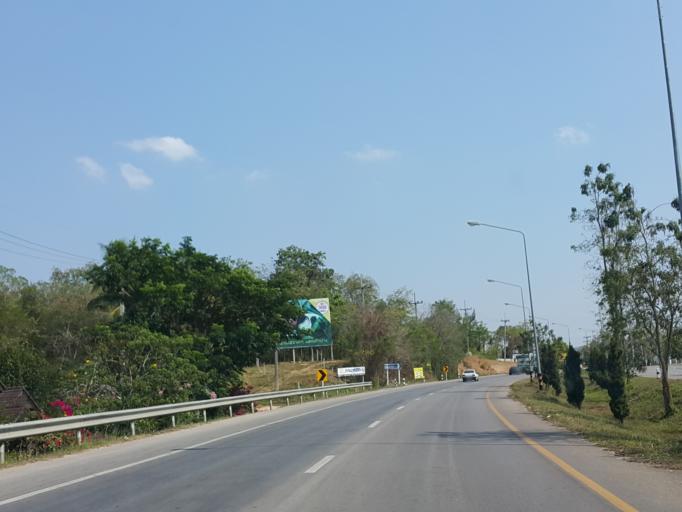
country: TH
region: Lampang
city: Lampang
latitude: 18.2838
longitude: 99.5178
